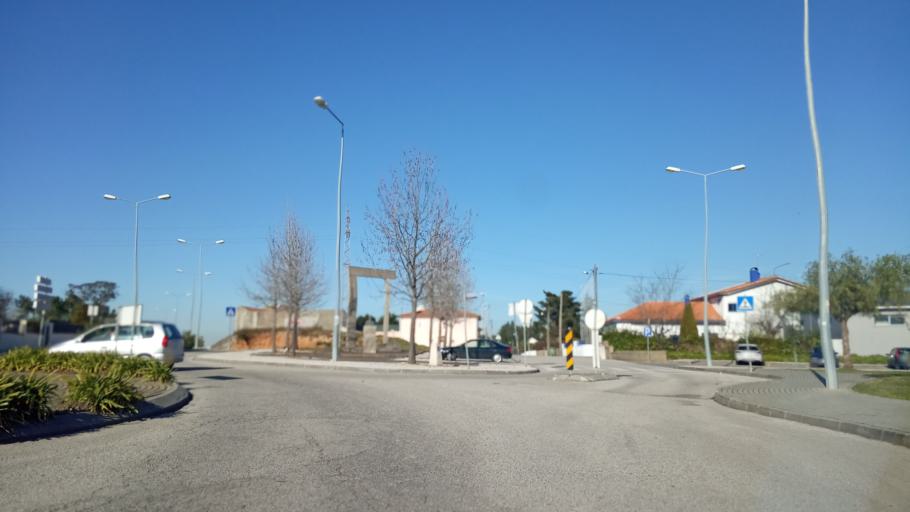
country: PT
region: Aveiro
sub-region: Anadia
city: Anadia
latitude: 40.4371
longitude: -8.4427
